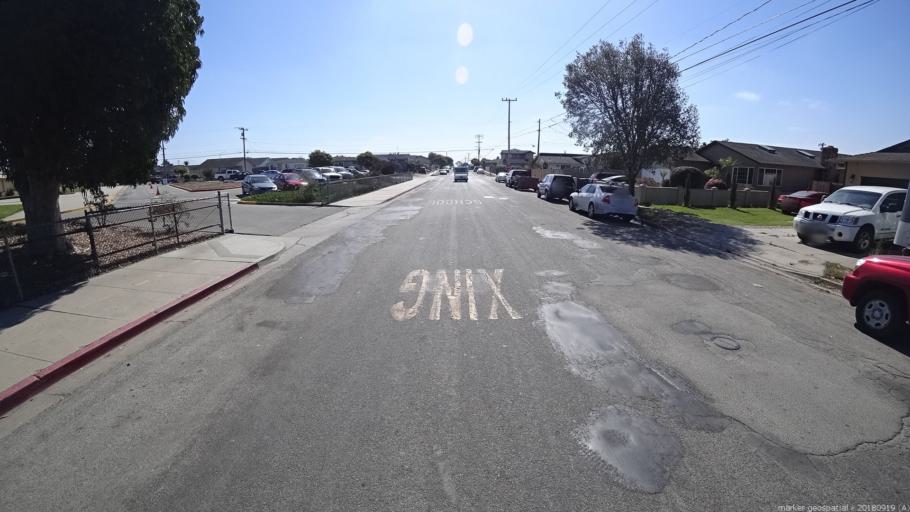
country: US
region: California
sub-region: Monterey County
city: Castroville
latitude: 36.7713
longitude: -121.7583
